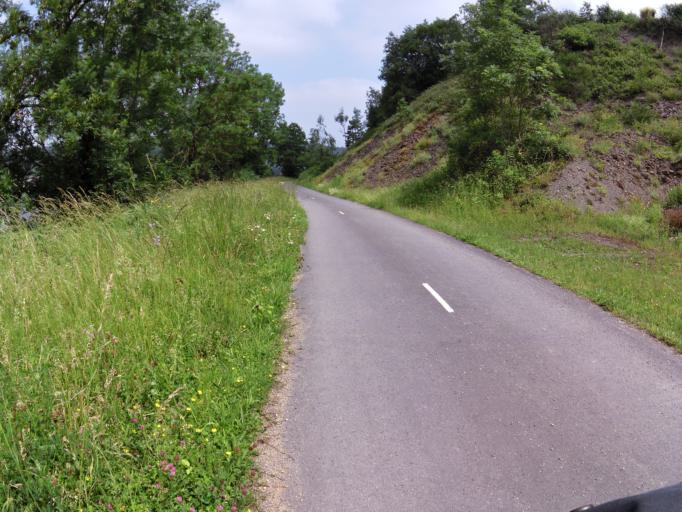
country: BE
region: Wallonia
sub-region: Province de Namur
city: Doische
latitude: 50.1046
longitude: 4.7671
